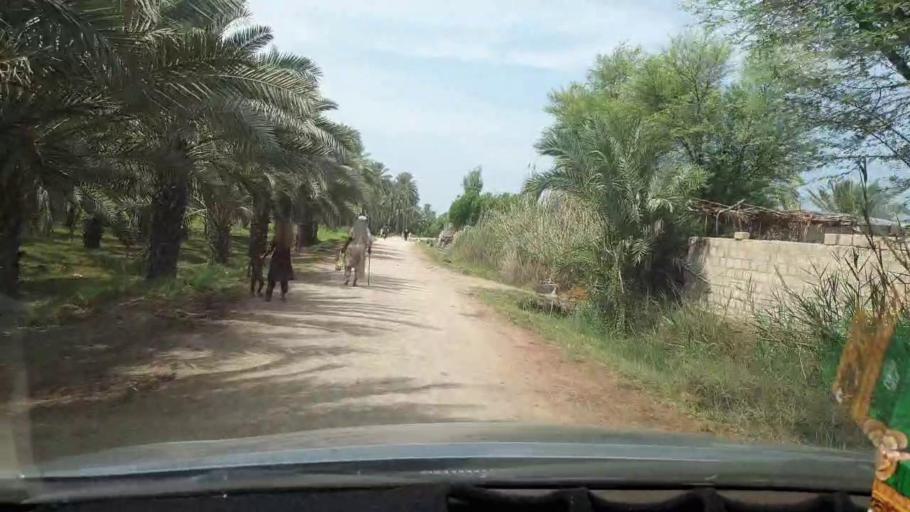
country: PK
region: Sindh
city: Khairpur
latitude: 27.4888
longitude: 68.7533
